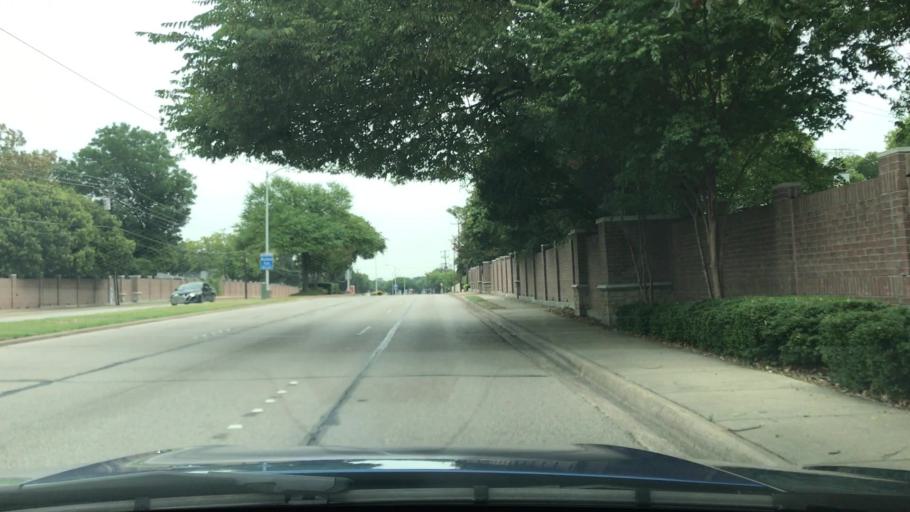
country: US
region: Texas
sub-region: Dallas County
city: Richardson
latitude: 32.9623
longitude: -96.7544
